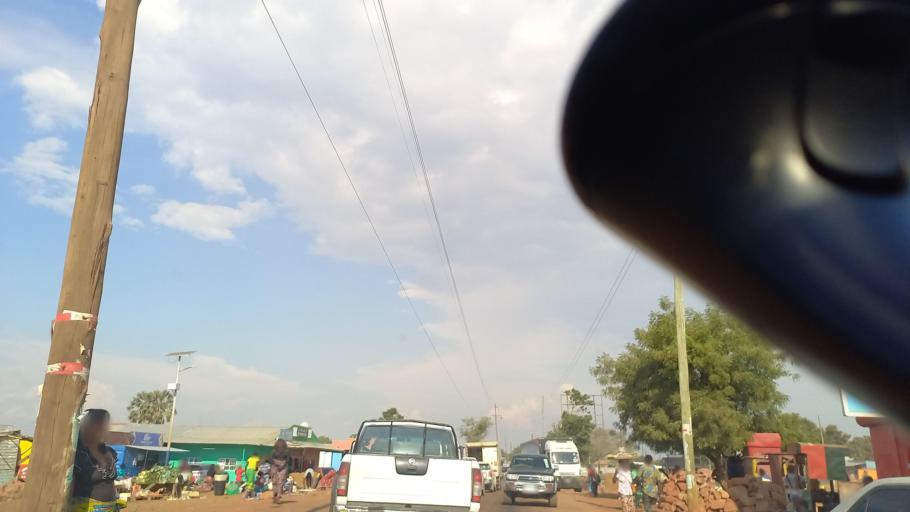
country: ZM
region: Southern
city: Mazabuka
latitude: -15.8524
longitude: 27.7505
